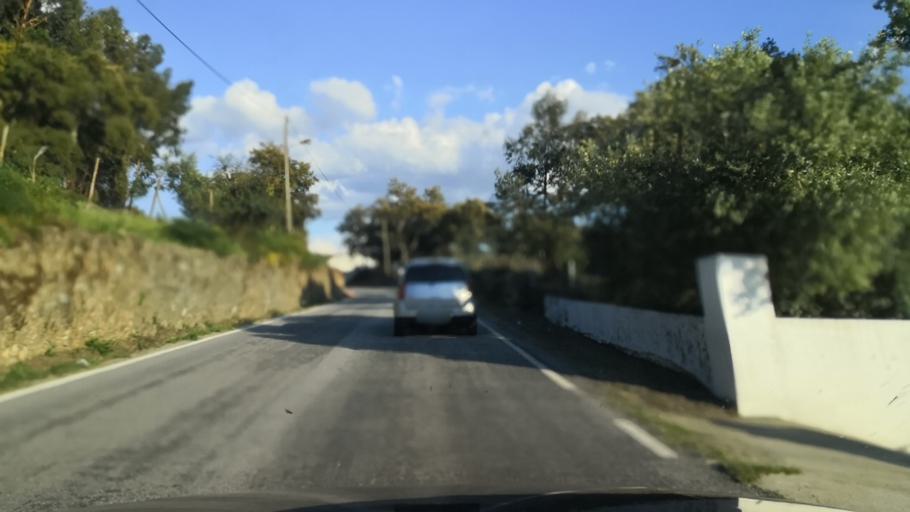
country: PT
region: Portalegre
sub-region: Portalegre
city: Portalegre
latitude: 39.3279
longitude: -7.4259
